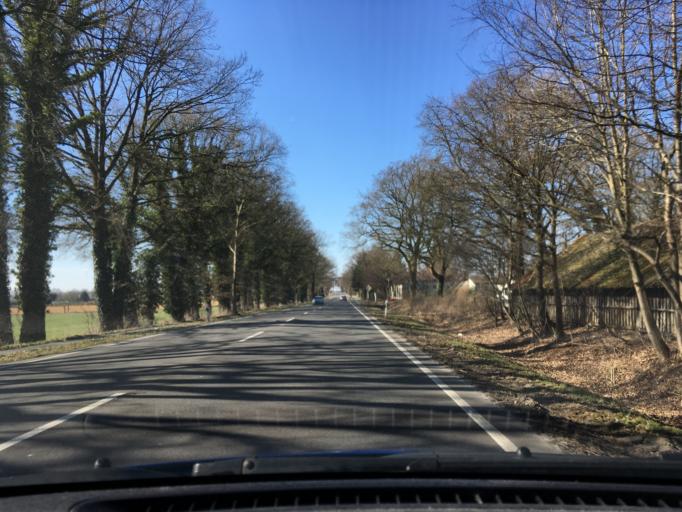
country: DE
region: Lower Saxony
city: Hassendorf
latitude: 53.1189
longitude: 9.2775
